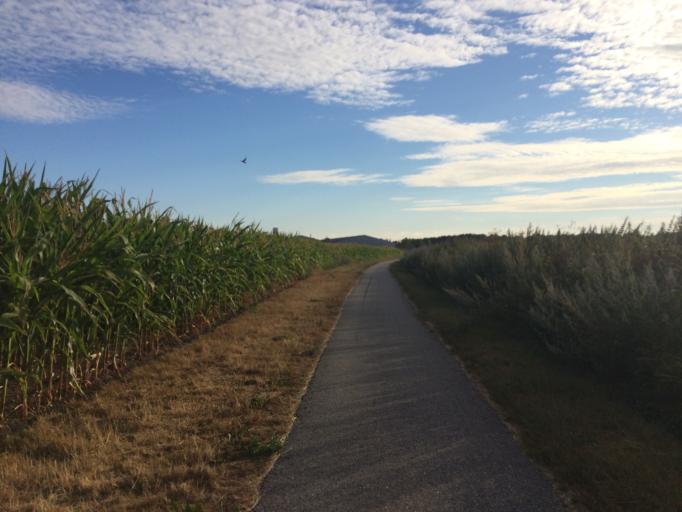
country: DK
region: Central Jutland
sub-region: Holstebro Kommune
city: Vinderup
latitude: 56.6095
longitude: 8.8704
